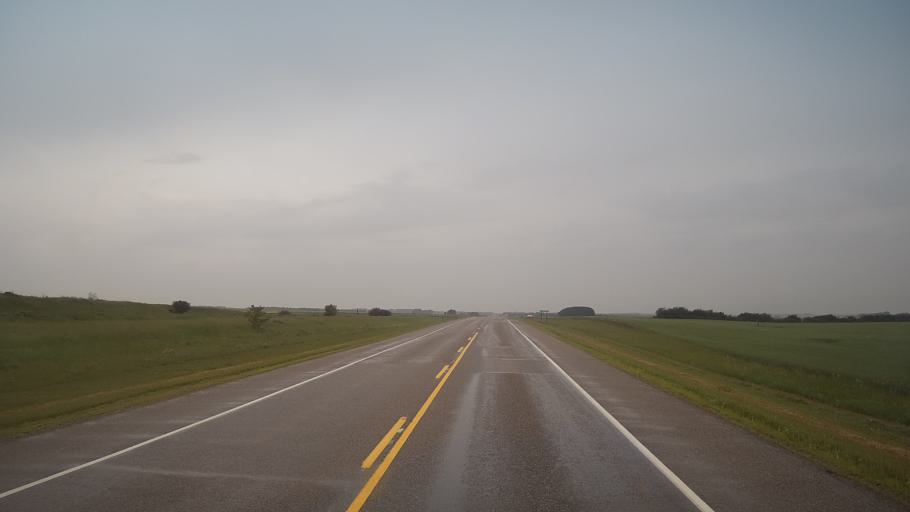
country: CA
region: Saskatchewan
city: Wilkie
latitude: 52.2232
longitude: -108.5219
